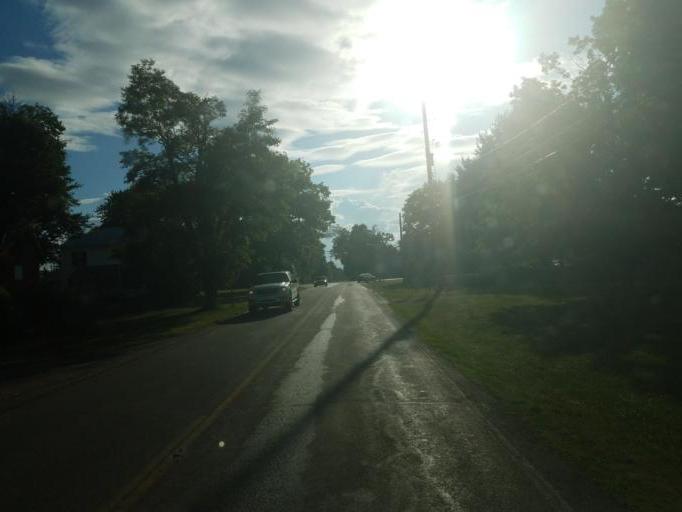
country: US
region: Indiana
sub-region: Steuben County
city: Fremont
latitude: 41.7967
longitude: -85.0039
